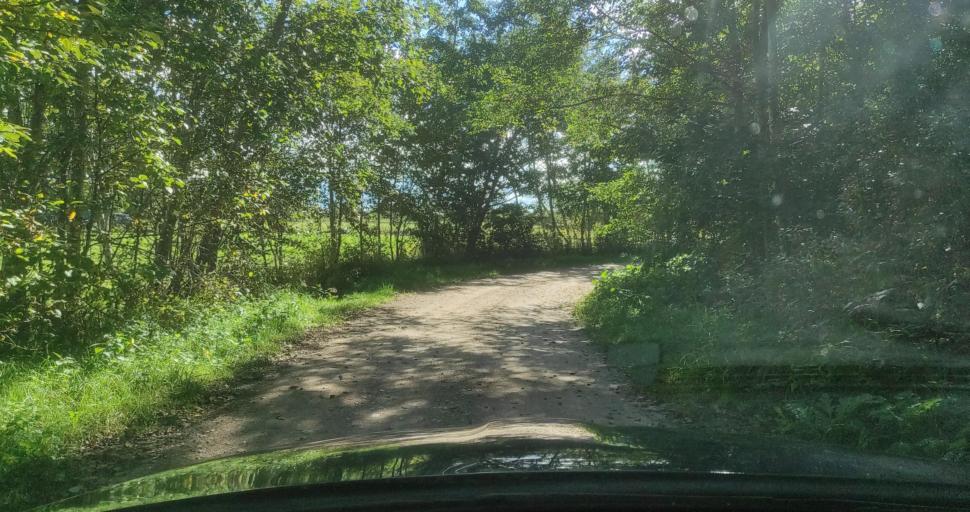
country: LV
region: Ventspils
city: Ventspils
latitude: 57.3687
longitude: 21.6317
